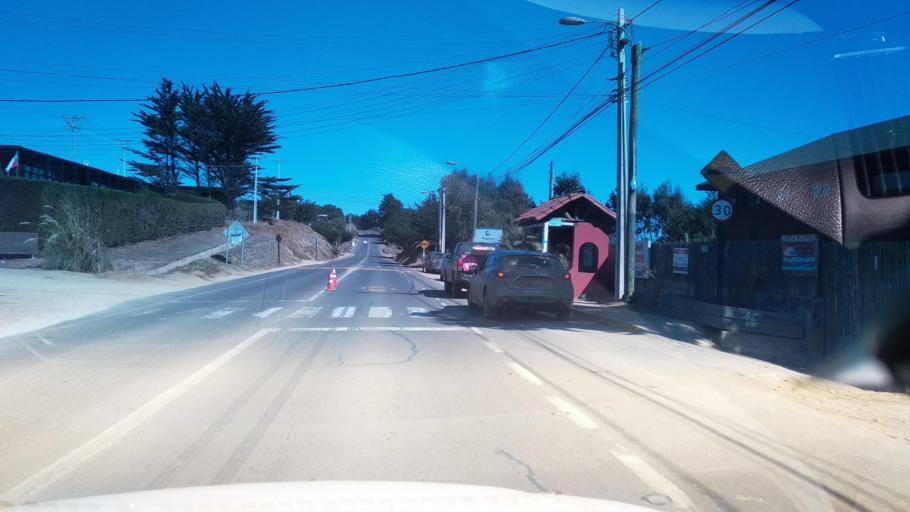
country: CL
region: O'Higgins
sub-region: Provincia de Colchagua
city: Santa Cruz
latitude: -34.4172
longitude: -72.0299
